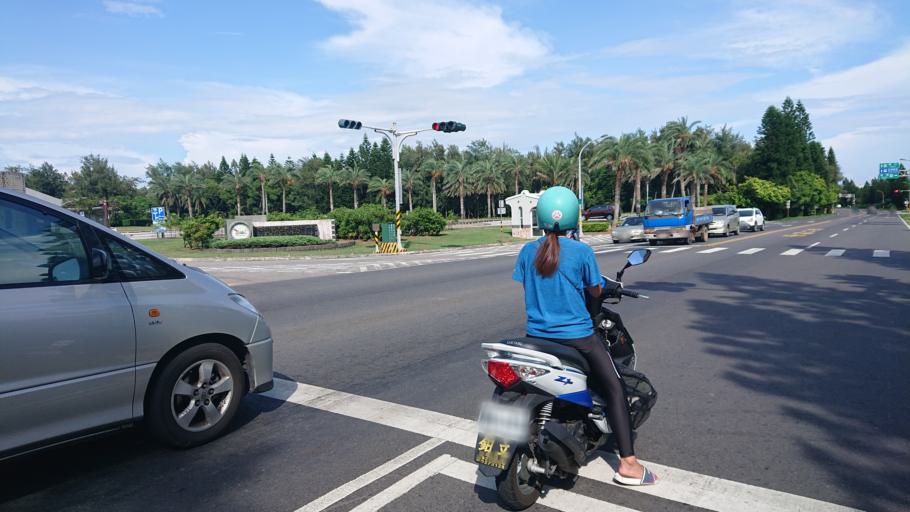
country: TW
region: Taiwan
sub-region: Penghu
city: Ma-kung
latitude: 23.5556
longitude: 119.6062
